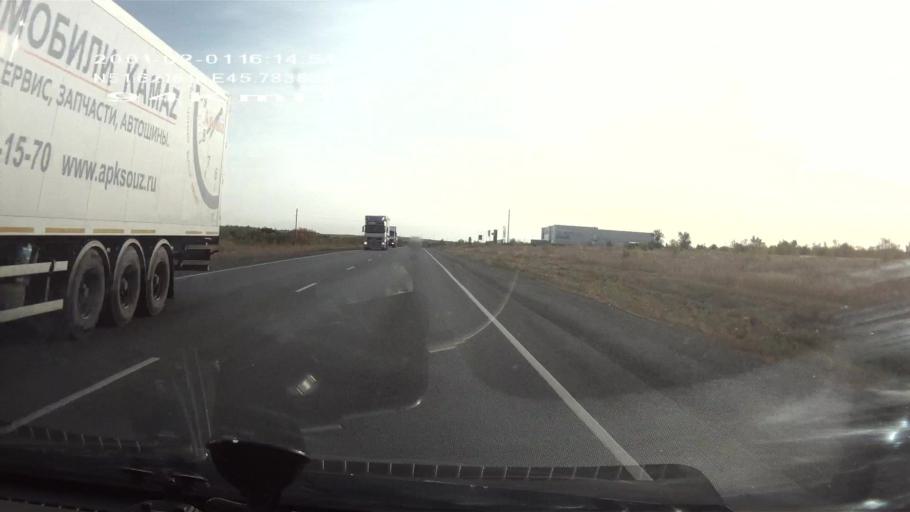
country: RU
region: Saratov
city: Sokolovyy
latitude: 51.6215
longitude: 45.7837
